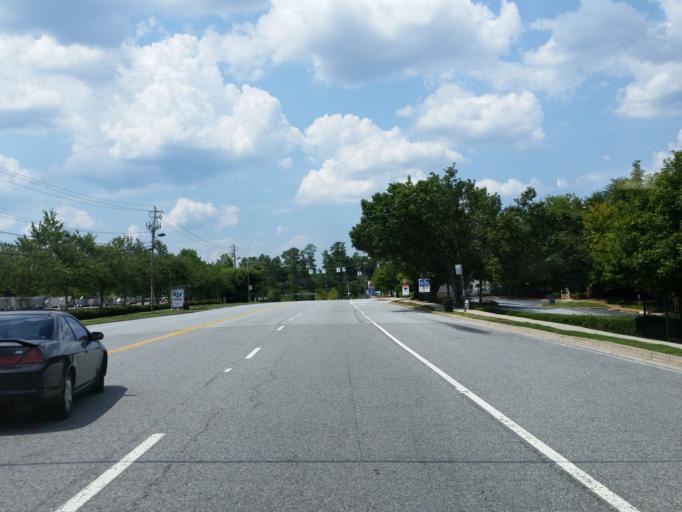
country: US
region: Georgia
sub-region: Fulton County
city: Roswell
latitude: 33.9951
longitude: -84.3490
